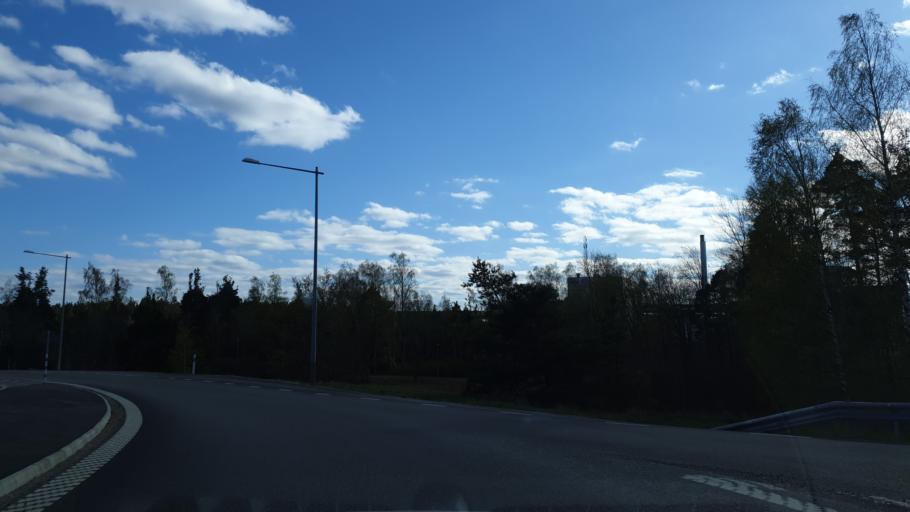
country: SE
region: Stockholm
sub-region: Sigtuna Kommun
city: Marsta
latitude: 59.6132
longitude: 17.8655
